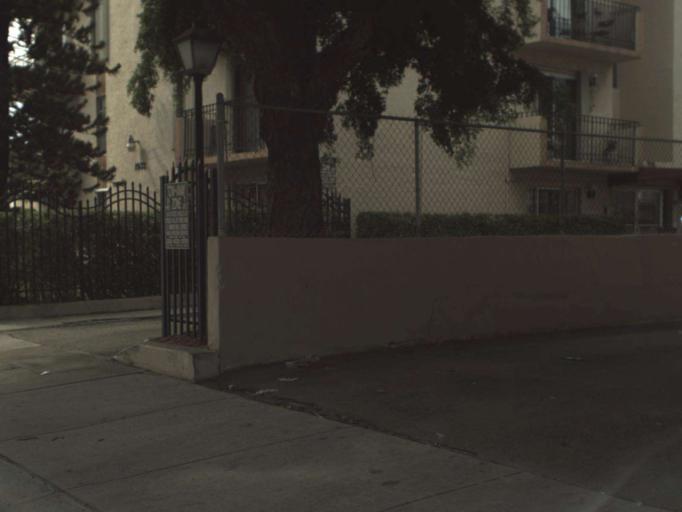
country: US
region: Florida
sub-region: Miami-Dade County
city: Miami
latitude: 25.7665
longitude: -80.2272
